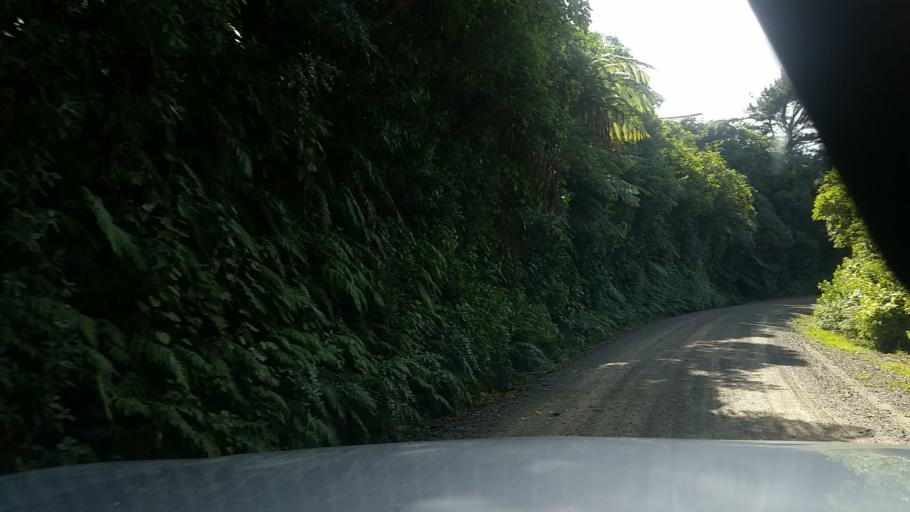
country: NZ
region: Marlborough
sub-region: Marlborough District
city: Picton
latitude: -41.2893
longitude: 174.1290
